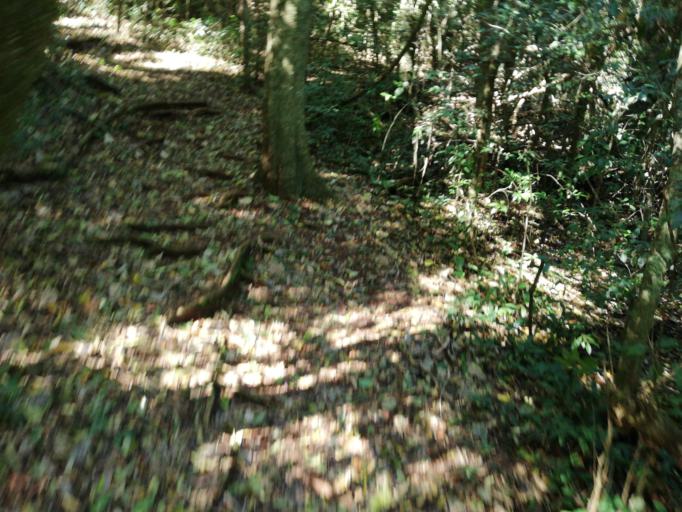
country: AR
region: Misiones
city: Aristobulo del Valle
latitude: -27.0619
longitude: -54.8289
